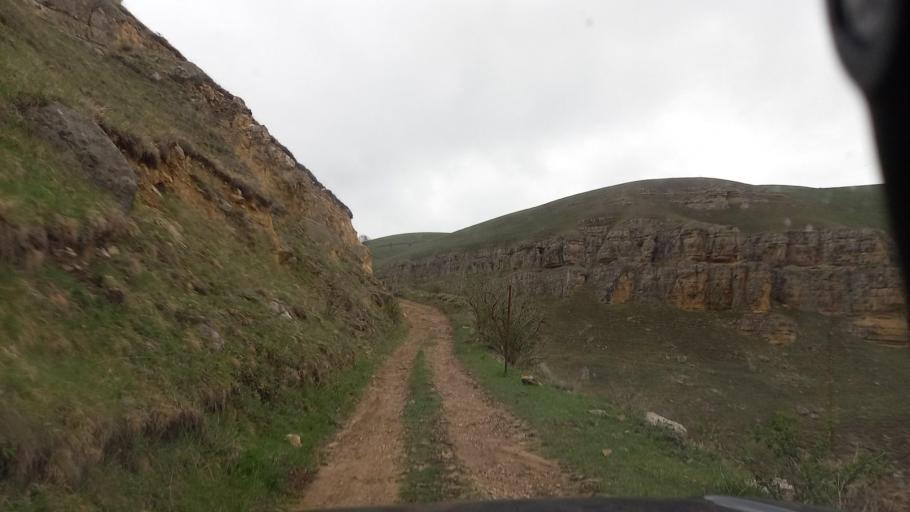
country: RU
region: Stavropol'skiy
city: Nezhinskiy
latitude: 43.8524
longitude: 42.6385
